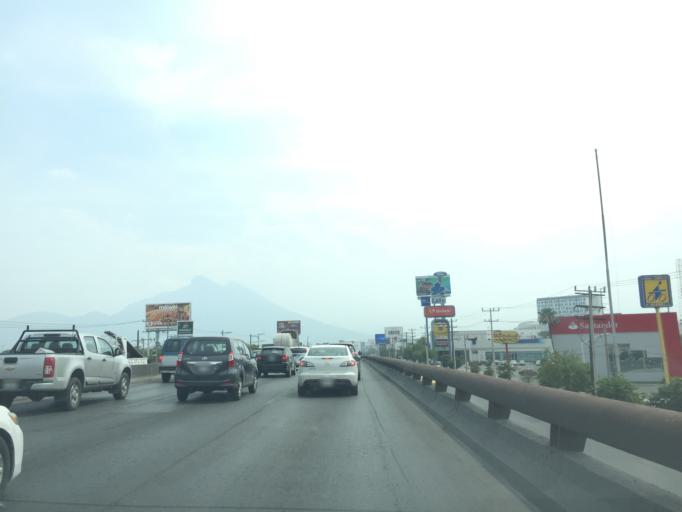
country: MX
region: Nuevo Leon
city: Guadalupe
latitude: 25.7237
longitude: -100.2146
